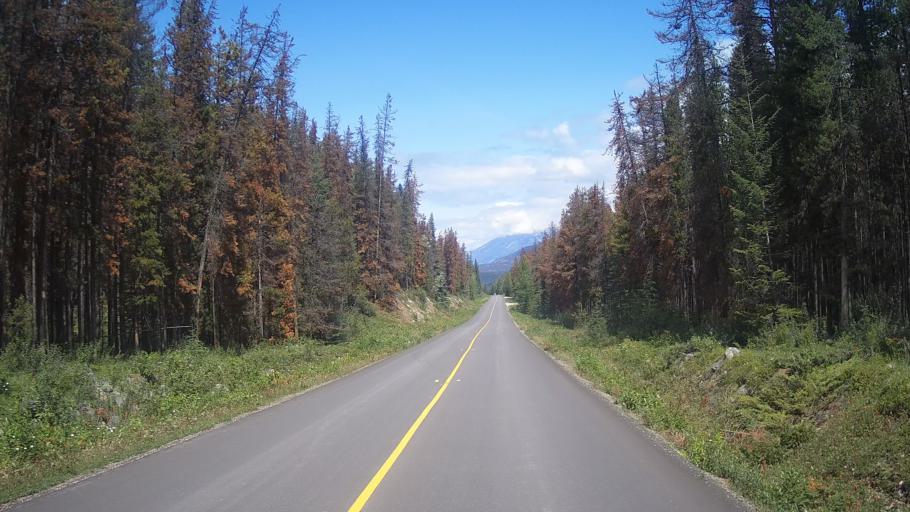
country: CA
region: Alberta
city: Jasper Park Lodge
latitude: 52.7777
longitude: -118.0325
